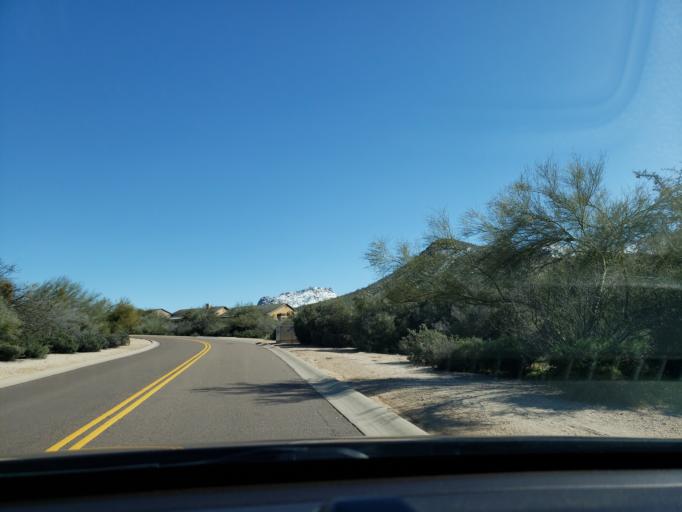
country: US
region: Arizona
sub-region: Maricopa County
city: Carefree
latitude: 33.7059
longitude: -111.8309
